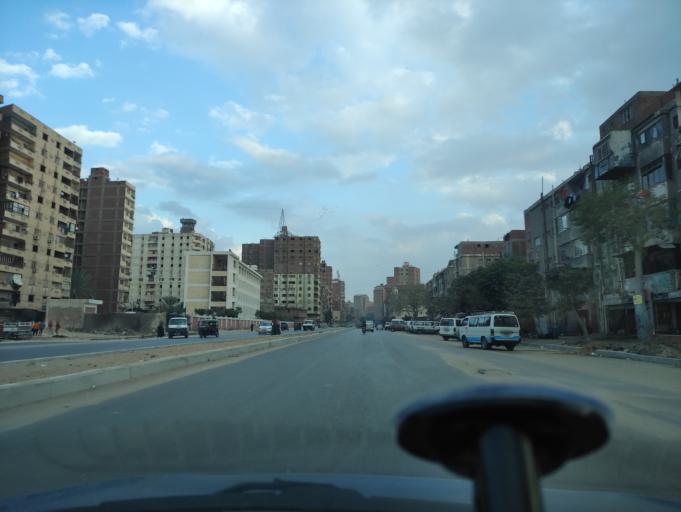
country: EG
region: Muhafazat al Qalyubiyah
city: Al Khankah
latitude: 30.1341
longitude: 31.3565
